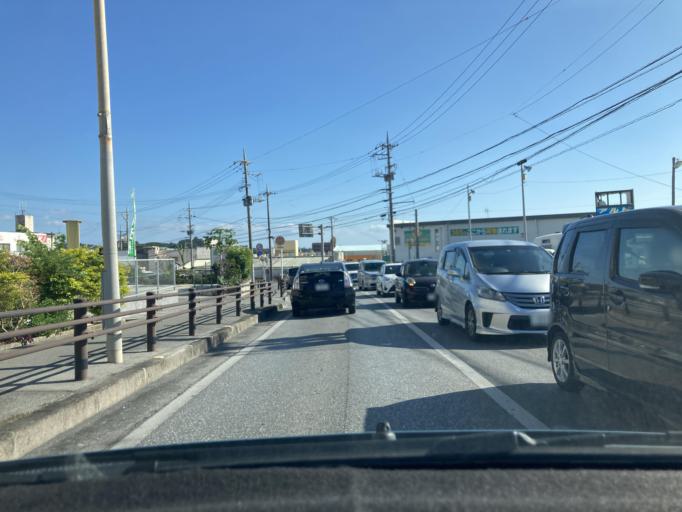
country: JP
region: Okinawa
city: Tomigusuku
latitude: 26.1807
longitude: 127.6635
